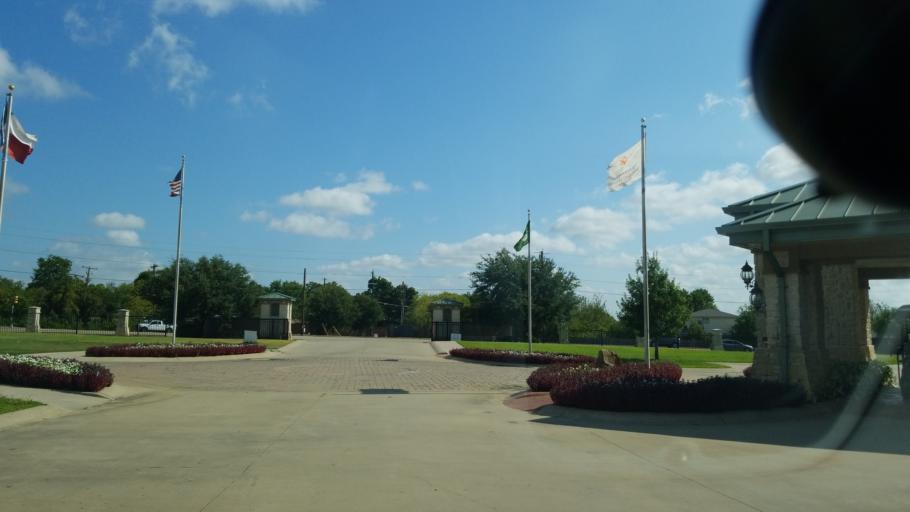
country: US
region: Texas
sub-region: Dallas County
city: Grand Prairie
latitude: 32.6979
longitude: -96.9920
